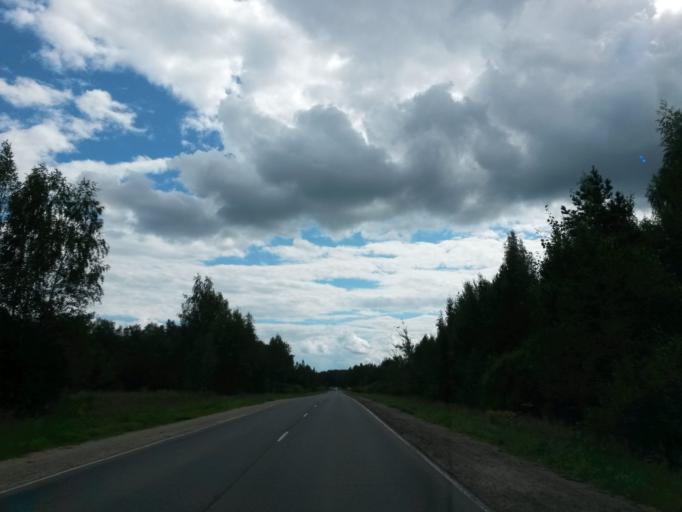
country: RU
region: Ivanovo
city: Pistsovo
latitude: 57.0983
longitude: 40.6572
